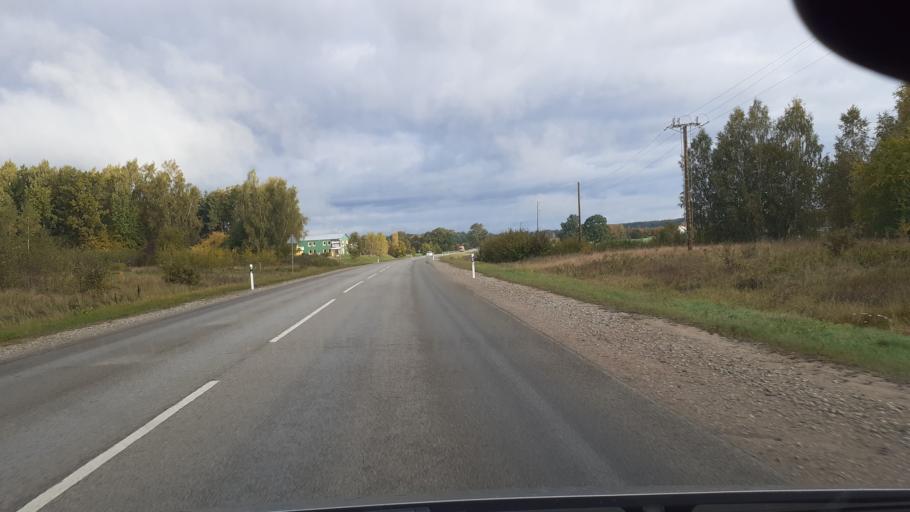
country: LV
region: Kuldigas Rajons
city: Kuldiga
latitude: 56.9707
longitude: 21.9328
